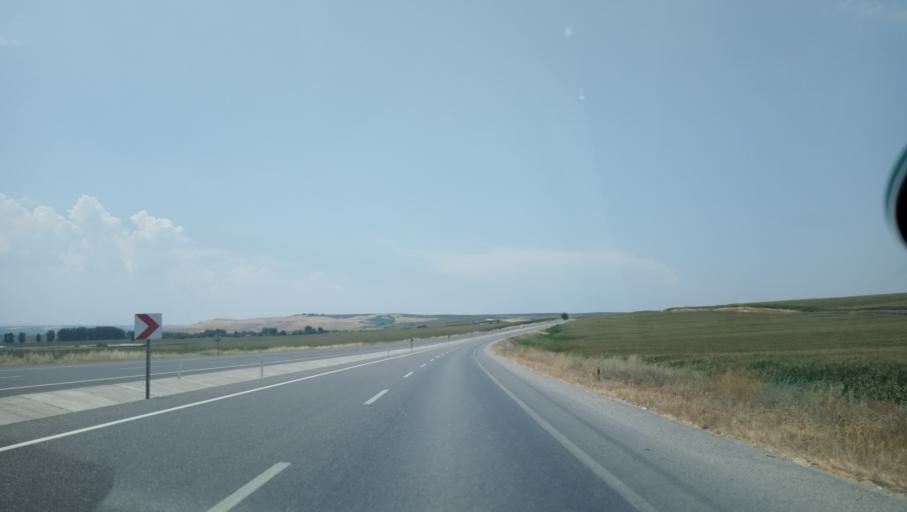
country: TR
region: Diyarbakir
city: Salat
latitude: 37.8472
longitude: 40.8429
